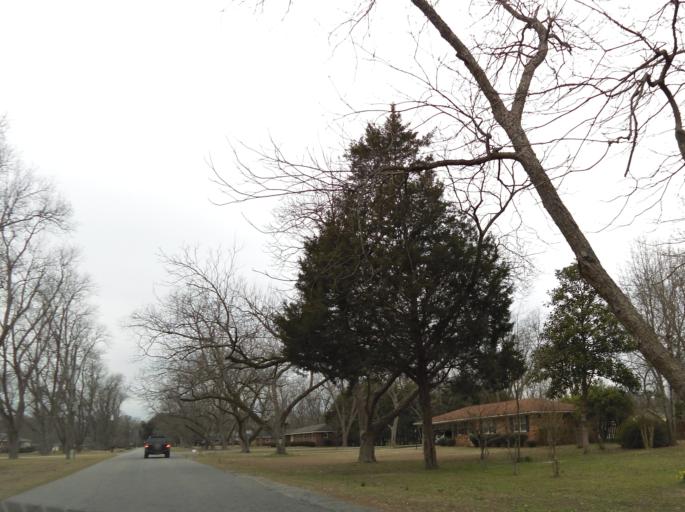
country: US
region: Georgia
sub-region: Houston County
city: Centerville
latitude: 32.7041
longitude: -83.6844
